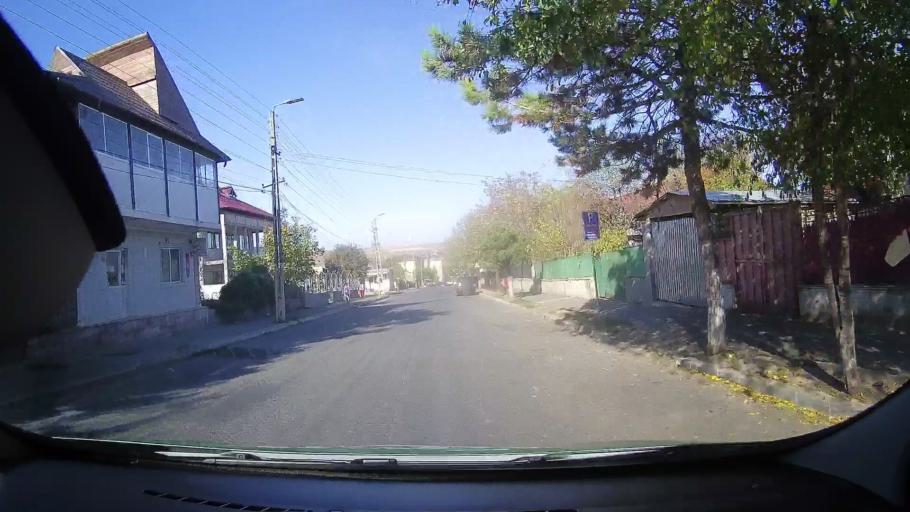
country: RO
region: Tulcea
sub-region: Oras Babadag
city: Babadag
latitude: 44.8912
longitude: 28.7272
